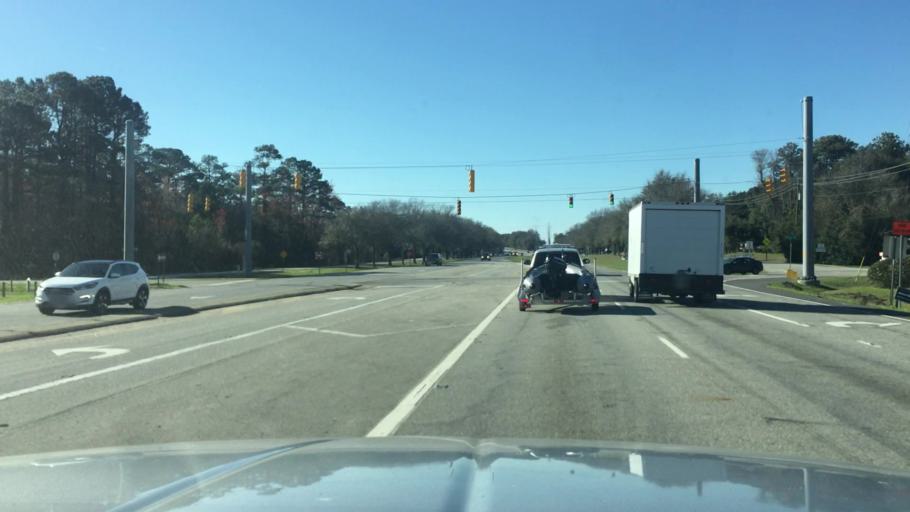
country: US
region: North Carolina
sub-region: New Hanover County
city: Sea Breeze
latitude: 34.0652
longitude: -77.8982
